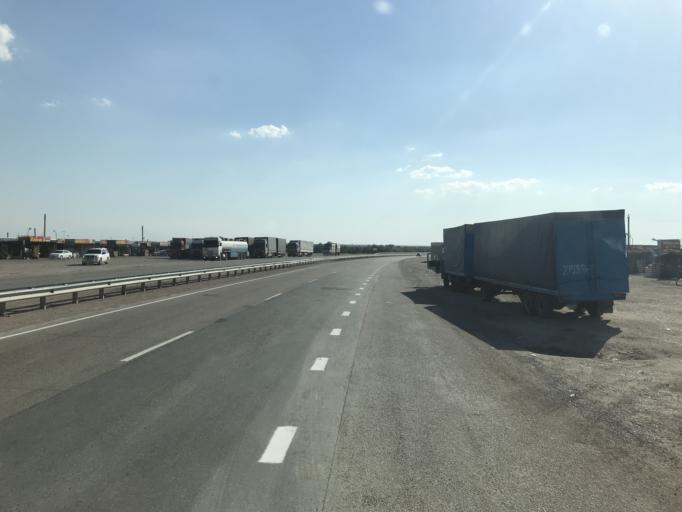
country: KG
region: Chuy
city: Sokuluk
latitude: 43.2692
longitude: 74.2226
